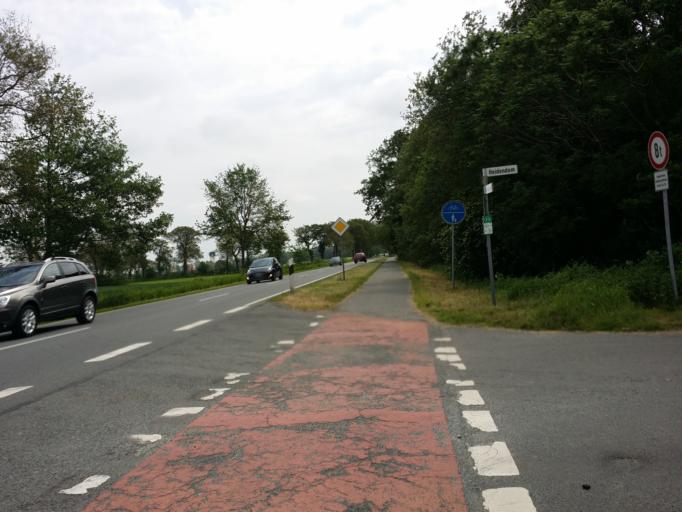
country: DE
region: Lower Saxony
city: Friedeburg
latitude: 53.4228
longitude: 7.8678
